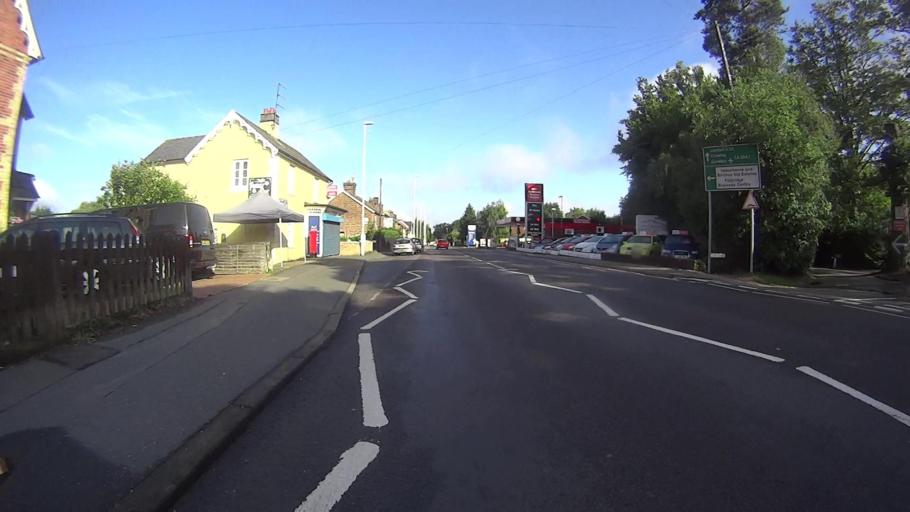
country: GB
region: England
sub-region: Surrey
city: Felbridge
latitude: 51.1362
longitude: -0.0320
